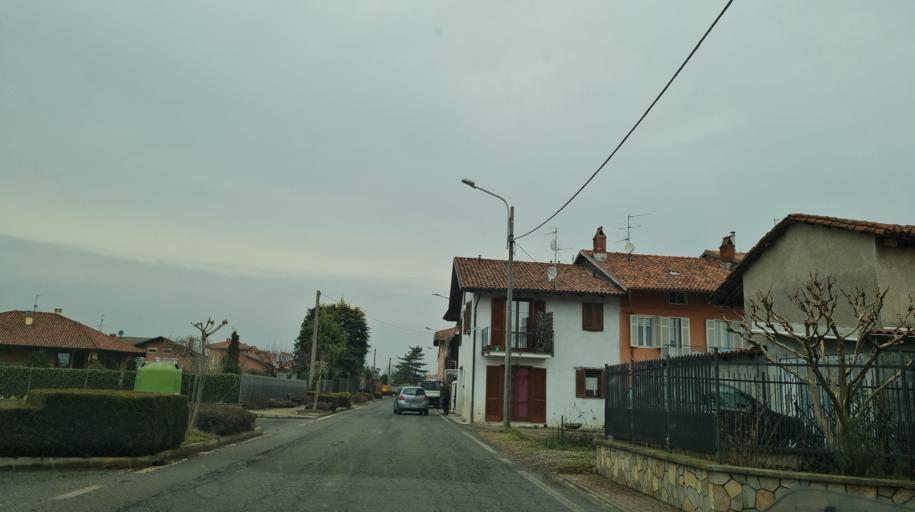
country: IT
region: Piedmont
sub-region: Provincia di Biella
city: Borriana
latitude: 45.5115
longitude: 8.0386
